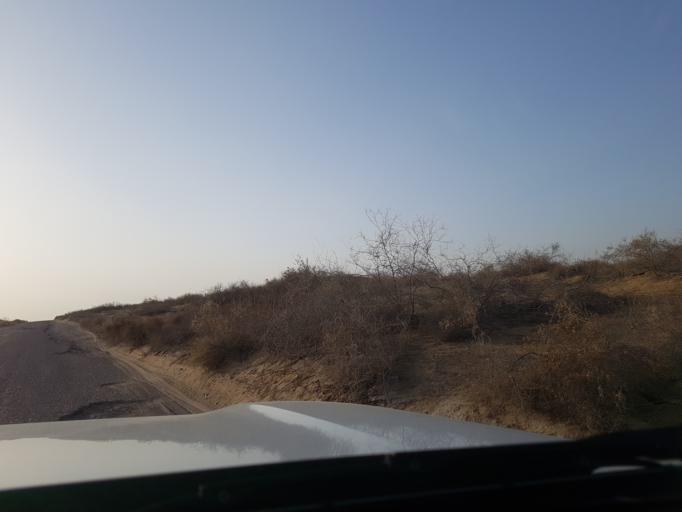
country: UZ
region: Xorazm
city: Khiwa
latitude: 41.1557
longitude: 60.6895
